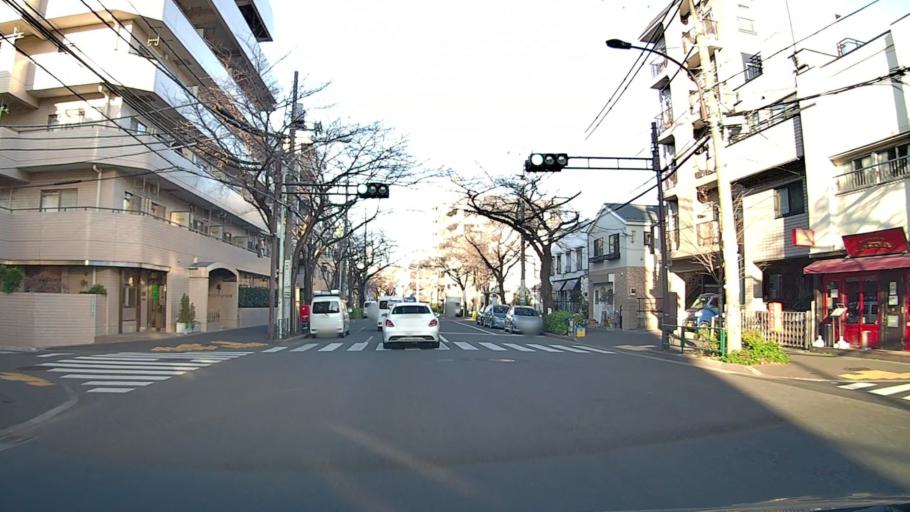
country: JP
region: Tokyo
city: Tokyo
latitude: 35.7182
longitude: 139.6696
